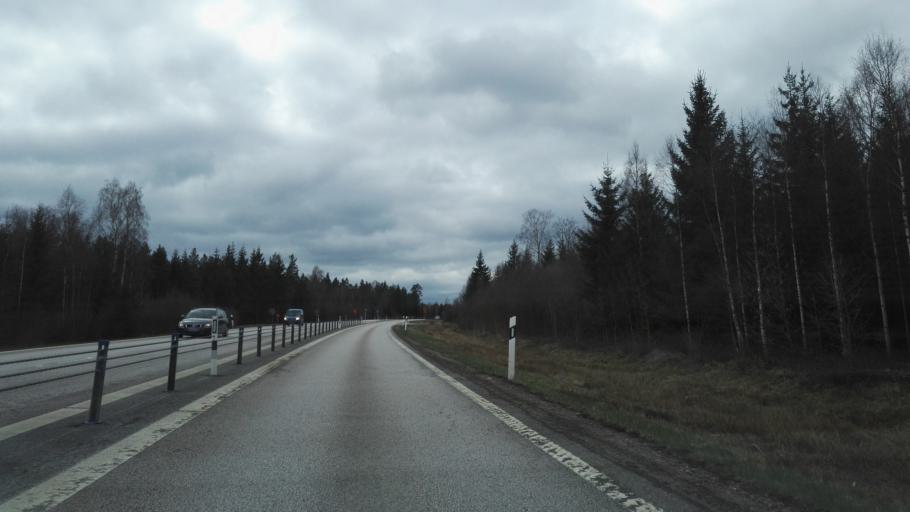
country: SE
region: Kronoberg
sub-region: Alvesta Kommun
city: Vislanda
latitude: 56.7380
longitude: 14.5048
